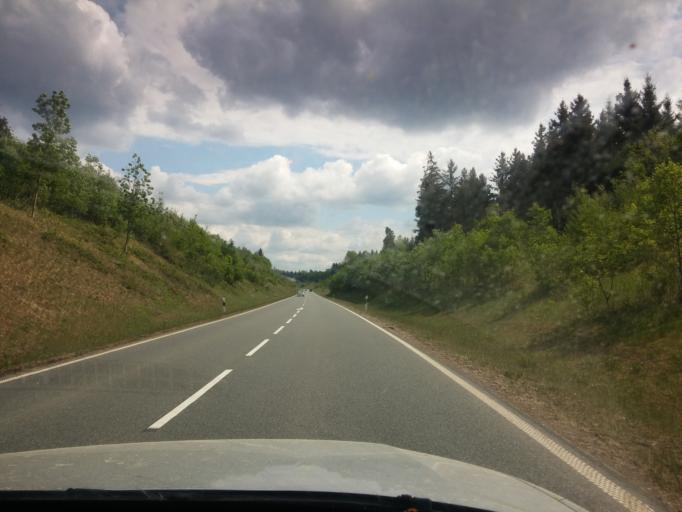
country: DE
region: Bavaria
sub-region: Upper Bavaria
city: Brunnthal
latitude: 48.0194
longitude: 11.6949
